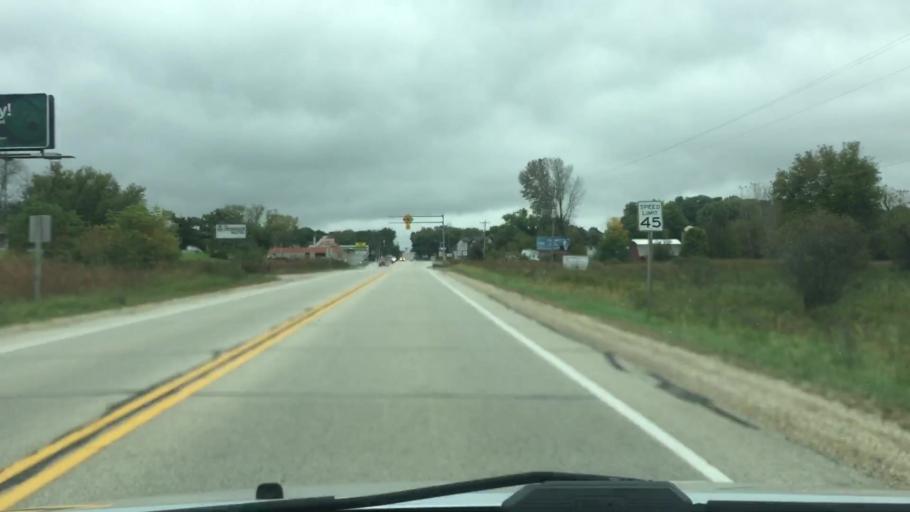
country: US
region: Wisconsin
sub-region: Walworth County
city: Elkhorn
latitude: 42.7283
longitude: -88.5428
